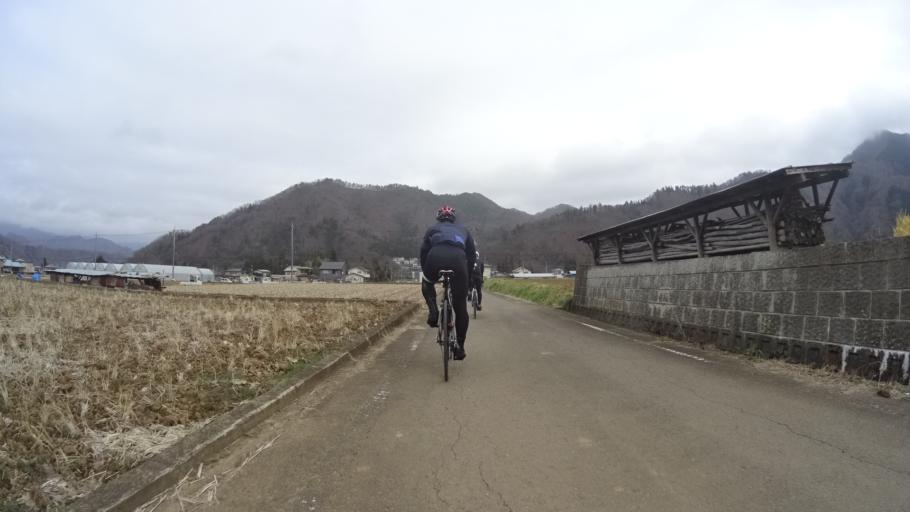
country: JP
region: Yamanashi
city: Otsuki
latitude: 35.5842
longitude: 138.9299
